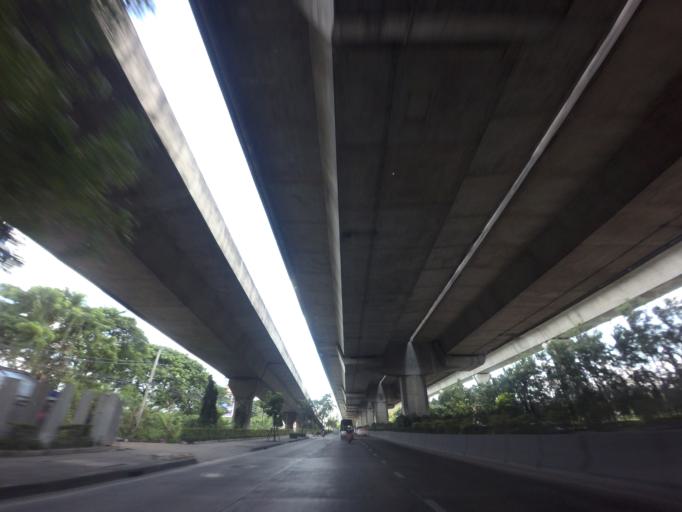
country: TH
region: Bangkok
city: Suan Luang
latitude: 13.7412
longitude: 100.6192
